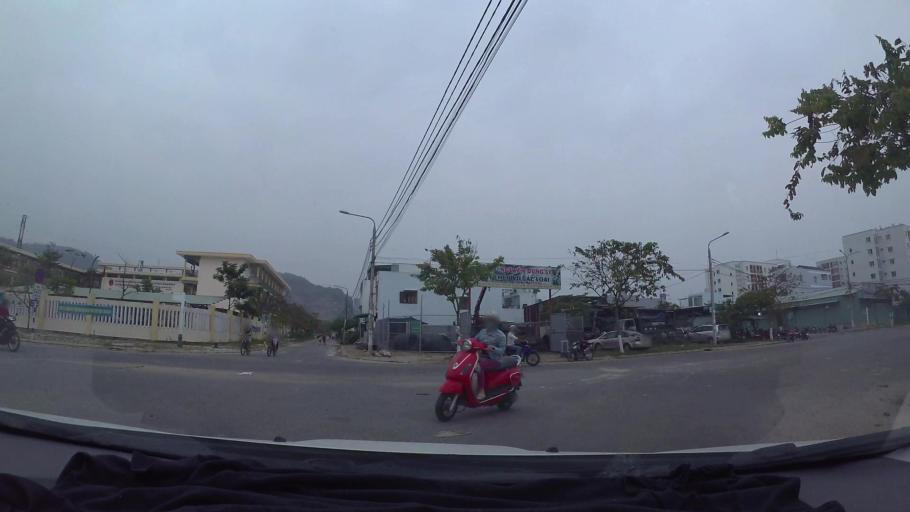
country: VN
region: Da Nang
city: Thanh Khe
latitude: 16.0433
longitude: 108.1766
